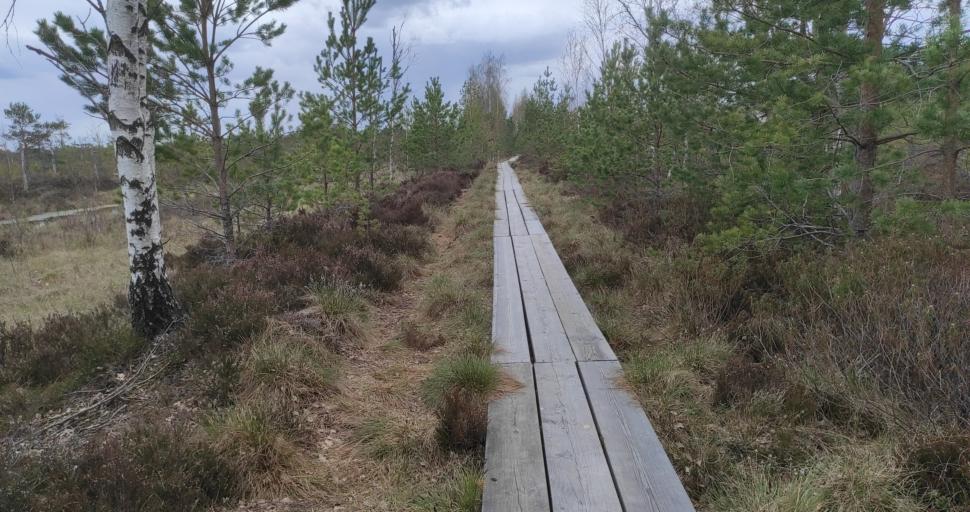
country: LV
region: Dundaga
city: Dundaga
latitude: 57.3552
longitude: 22.1538
